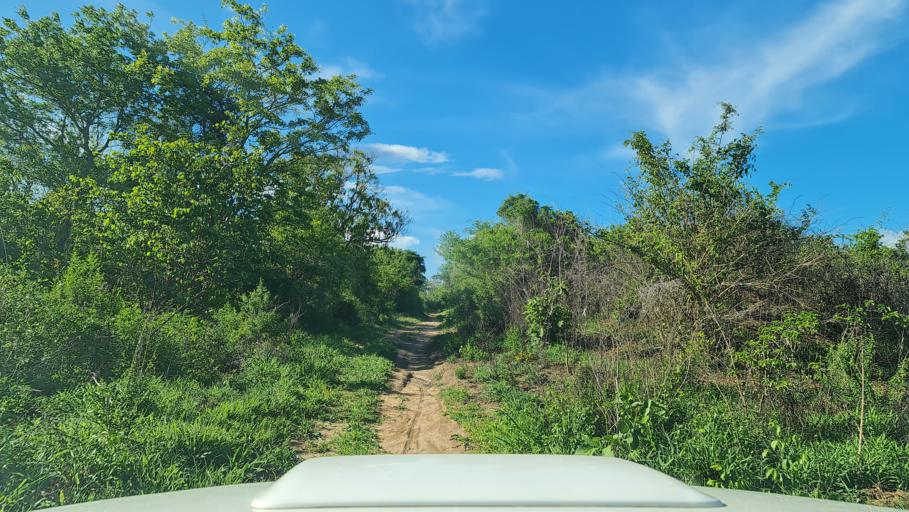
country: MZ
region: Nampula
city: Ilha de Mocambique
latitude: -15.2534
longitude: 40.1819
